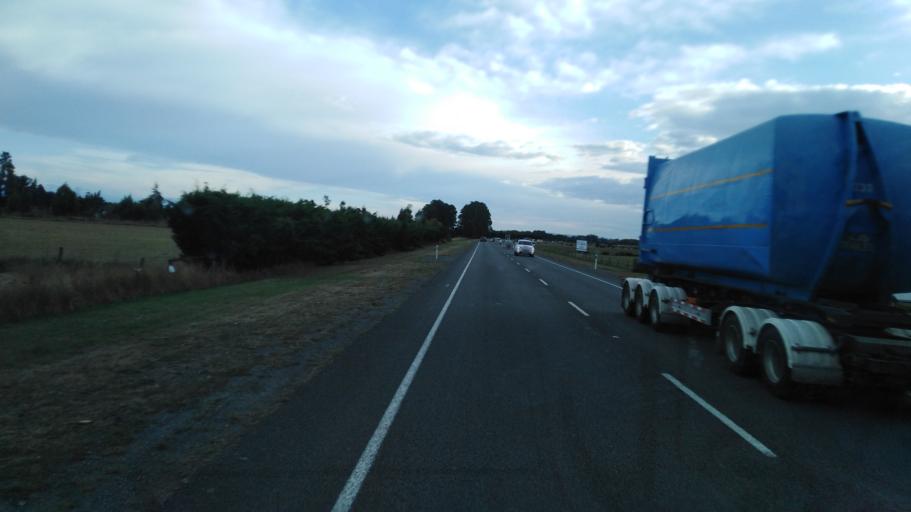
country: NZ
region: Canterbury
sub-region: Waimakariri District
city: Kaiapoi
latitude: -43.3664
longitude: 172.6502
